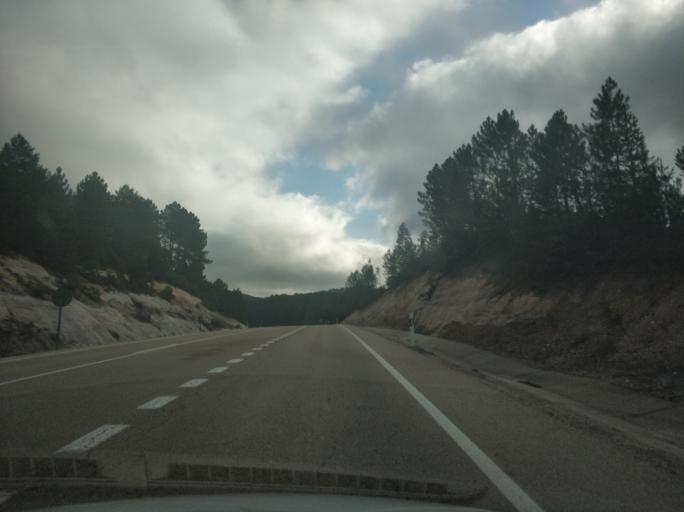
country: ES
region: Castille and Leon
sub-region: Provincia de Soria
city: Navaleno
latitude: 41.8304
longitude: -2.9781
